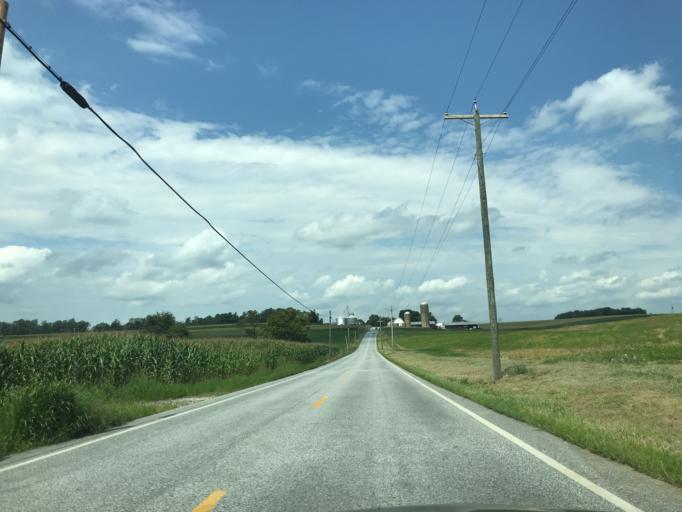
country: US
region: Pennsylvania
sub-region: York County
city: New Freedom
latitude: 39.6912
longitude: -76.7409
